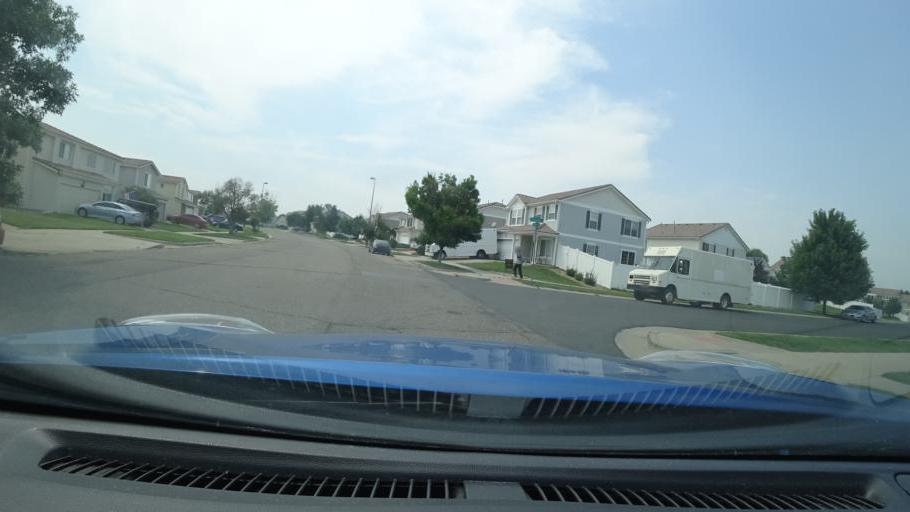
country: US
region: Colorado
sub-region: Adams County
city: Aurora
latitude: 39.7751
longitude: -104.7375
